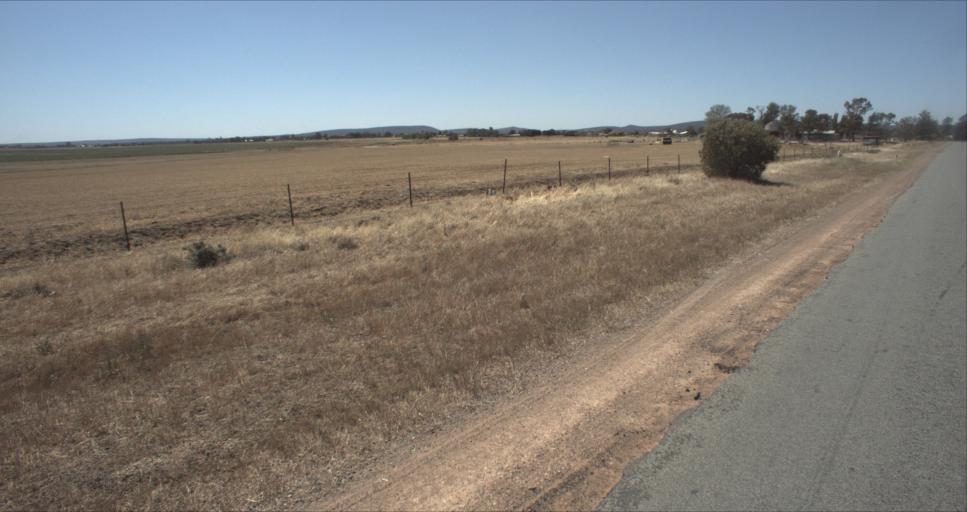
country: AU
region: New South Wales
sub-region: Leeton
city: Leeton
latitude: -34.5407
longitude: 146.4381
